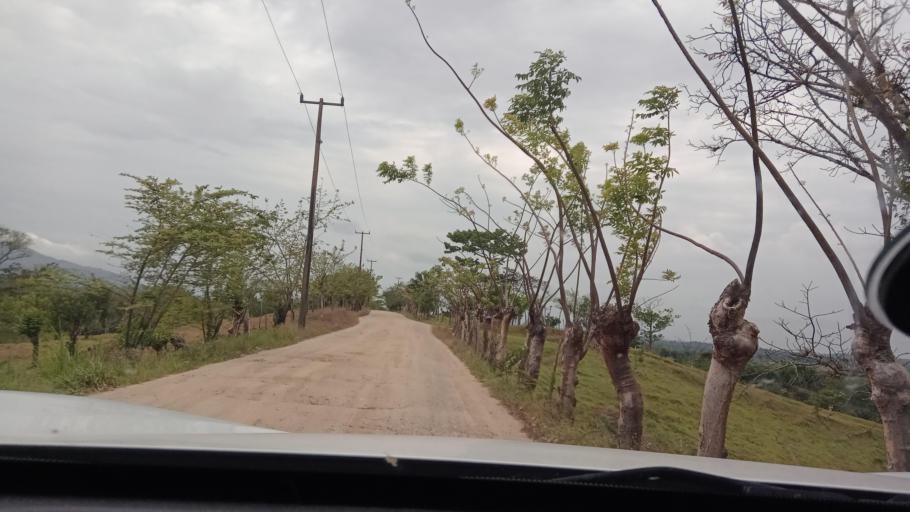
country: MX
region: Tabasco
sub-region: Huimanguillo
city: Francisco Rueda
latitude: 17.5807
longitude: -94.0736
